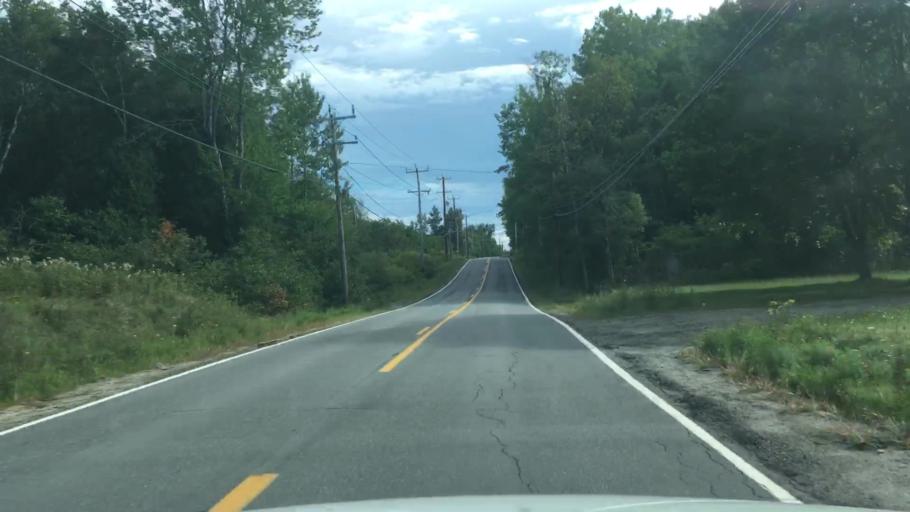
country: US
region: Maine
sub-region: Hancock County
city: Ellsworth
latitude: 44.4911
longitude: -68.4202
